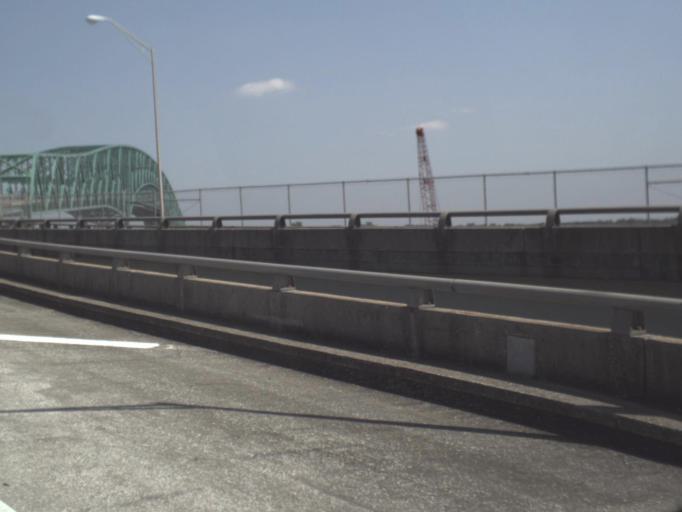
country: US
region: Florida
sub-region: Duval County
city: Jacksonville
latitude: 30.3202
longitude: -81.6316
